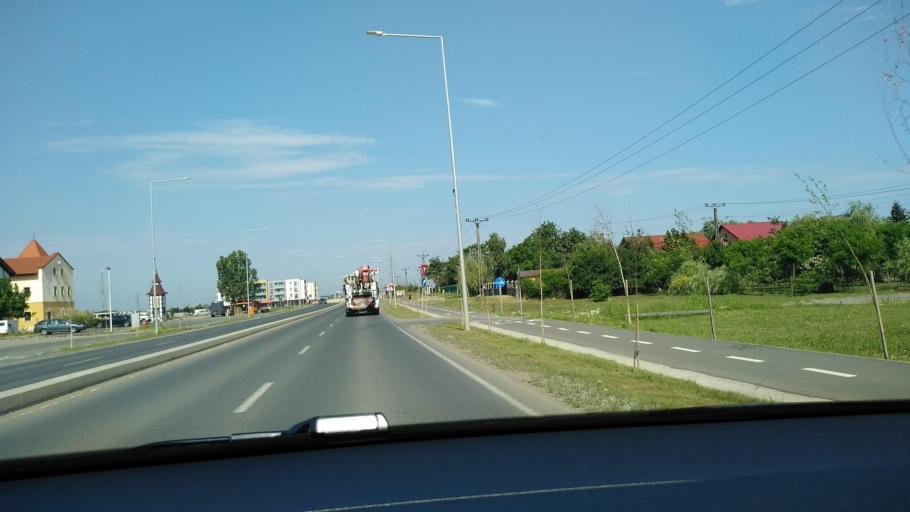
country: RO
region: Timis
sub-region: Comuna Mosnita Noua
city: Mosnita Noua
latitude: 45.7235
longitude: 21.2971
